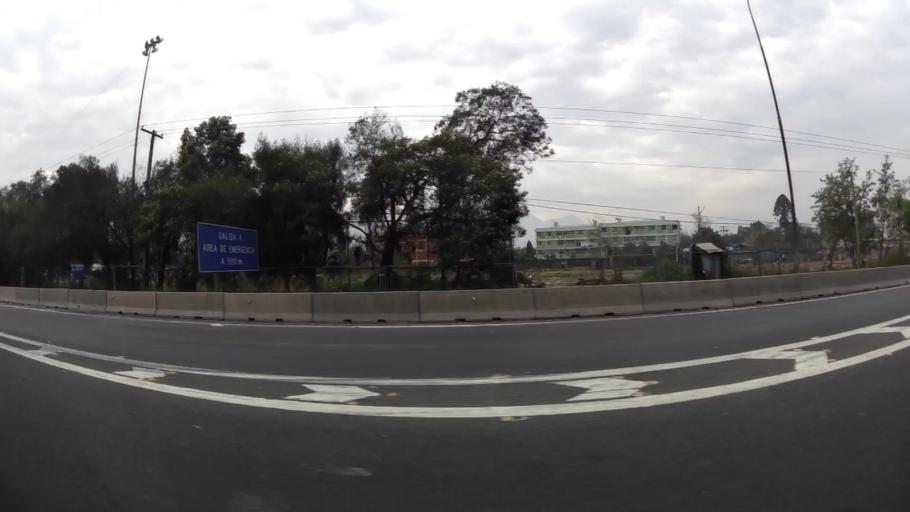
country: CL
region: Santiago Metropolitan
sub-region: Provincia de Santiago
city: Lo Prado
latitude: -33.3773
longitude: -70.6951
